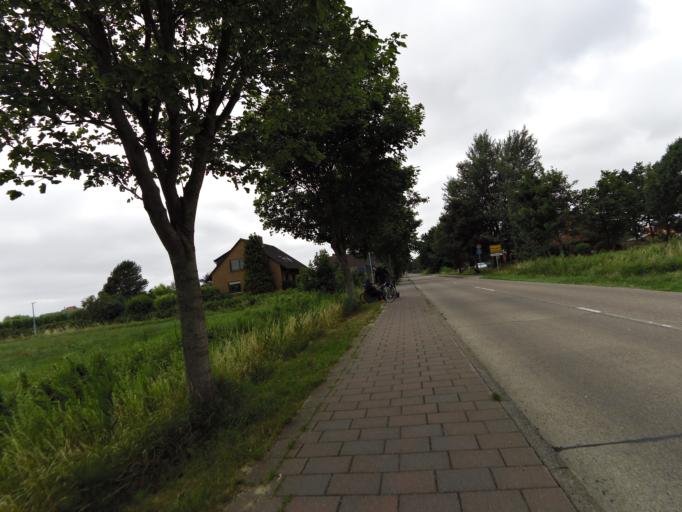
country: DE
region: Lower Saxony
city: Padingbuttel
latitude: 53.7308
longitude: 8.5286
